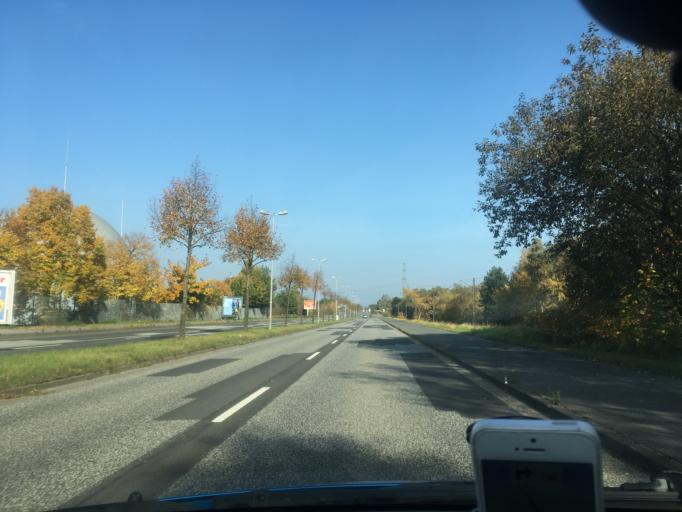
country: DE
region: Mecklenburg-Vorpommern
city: Feldstadt
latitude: 53.5788
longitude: 11.3983
